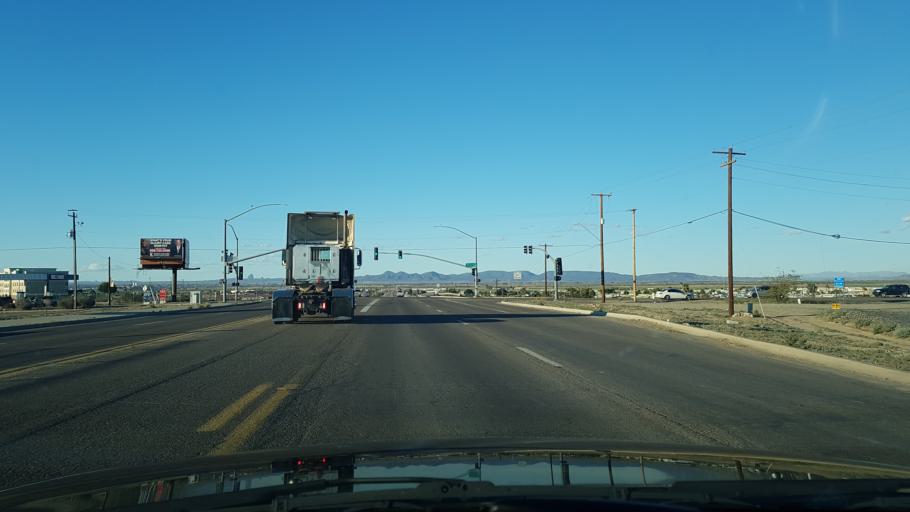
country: US
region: Arizona
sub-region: Yuma County
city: Yuma
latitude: 32.6903
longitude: -114.5988
